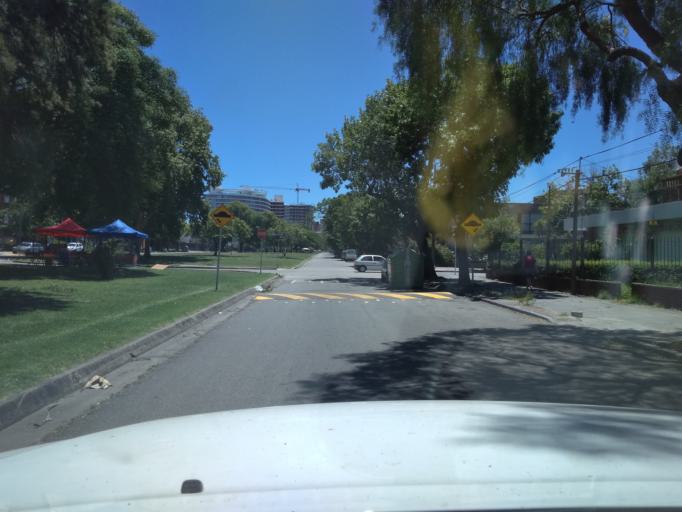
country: UY
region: Canelones
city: Paso de Carrasco
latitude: -34.8914
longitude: -56.1062
